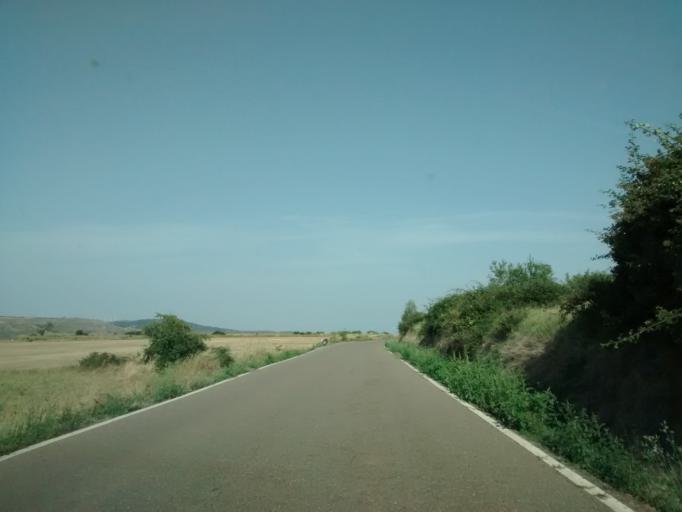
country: ES
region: Aragon
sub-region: Provincia de Zaragoza
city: Trasmoz
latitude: 41.8275
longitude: -1.7114
